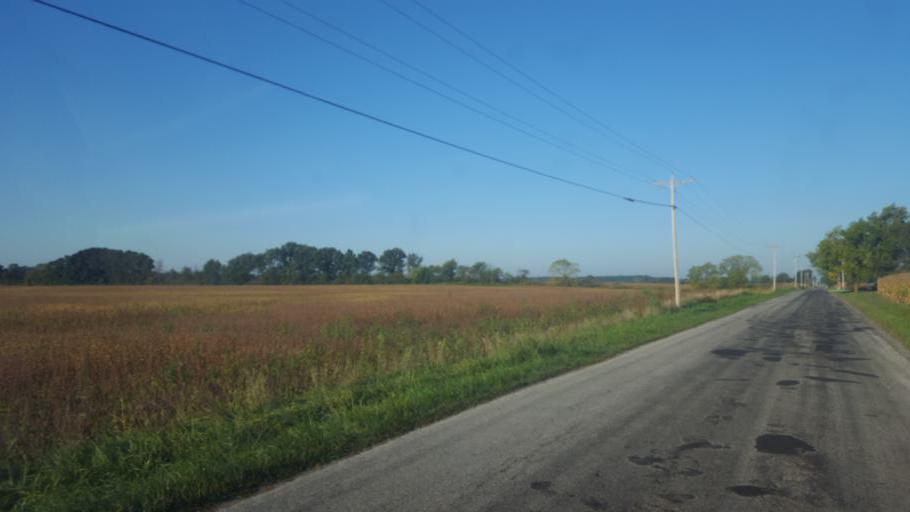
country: US
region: Ohio
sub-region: Morrow County
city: Cardington
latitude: 40.5574
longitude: -82.9021
